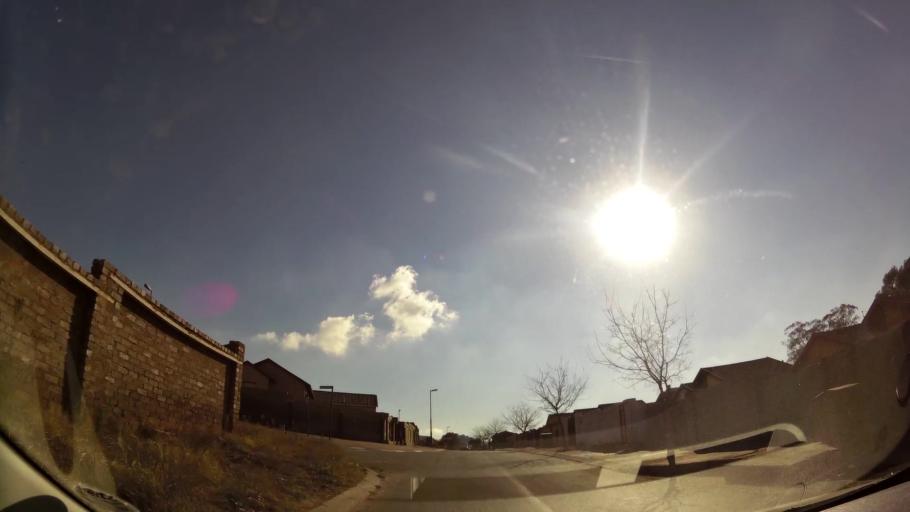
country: ZA
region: Gauteng
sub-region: City of Johannesburg Metropolitan Municipality
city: Roodepoort
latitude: -26.1584
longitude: 27.8357
